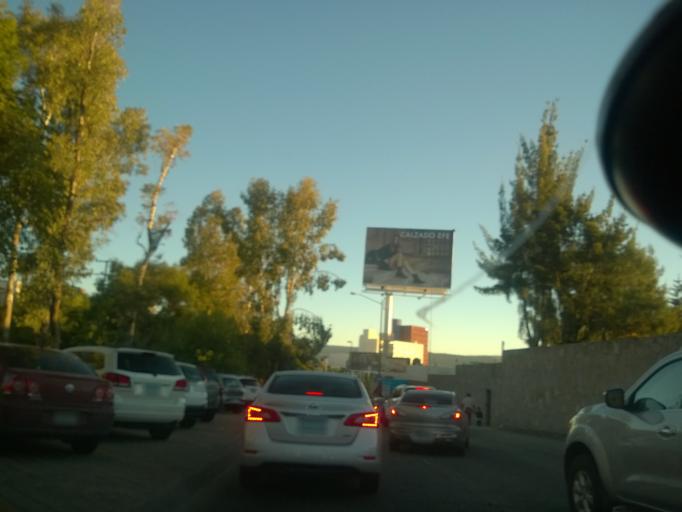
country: MX
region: Guanajuato
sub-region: Leon
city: La Ermita
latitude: 21.1535
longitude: -101.7025
